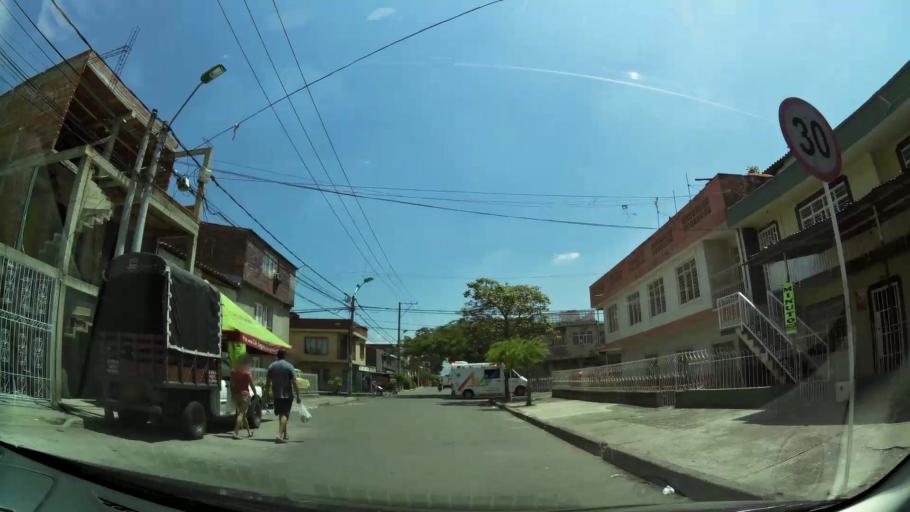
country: CO
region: Valle del Cauca
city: Cali
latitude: 3.4362
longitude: -76.5020
